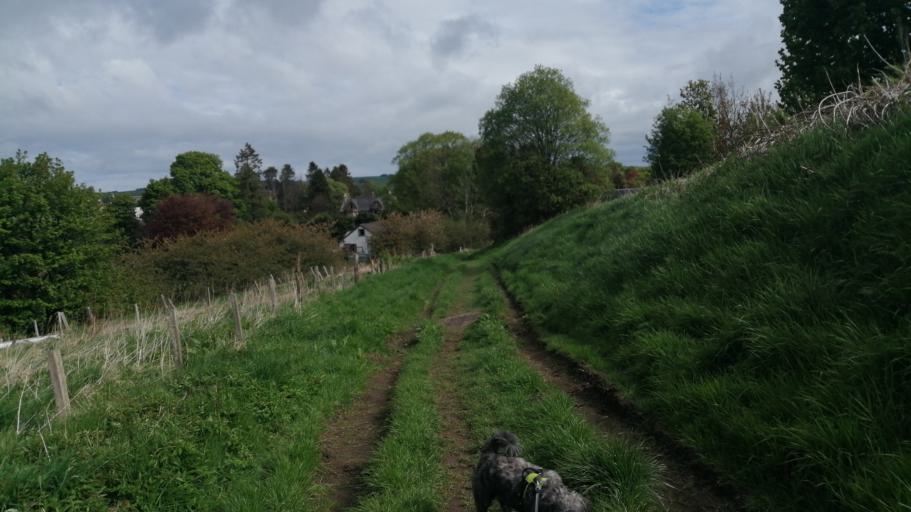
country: GB
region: Scotland
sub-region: Moray
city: Keith
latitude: 57.5405
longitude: -2.9593
